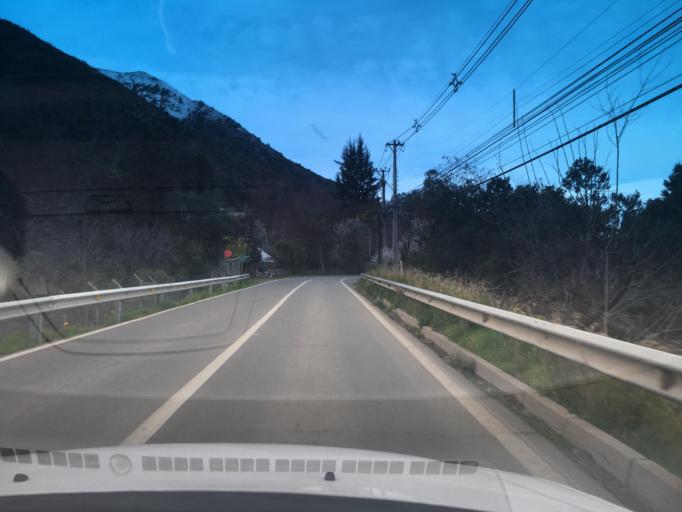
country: CL
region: Santiago Metropolitan
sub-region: Provincia de Cordillera
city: Puente Alto
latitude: -33.5756
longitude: -70.4465
